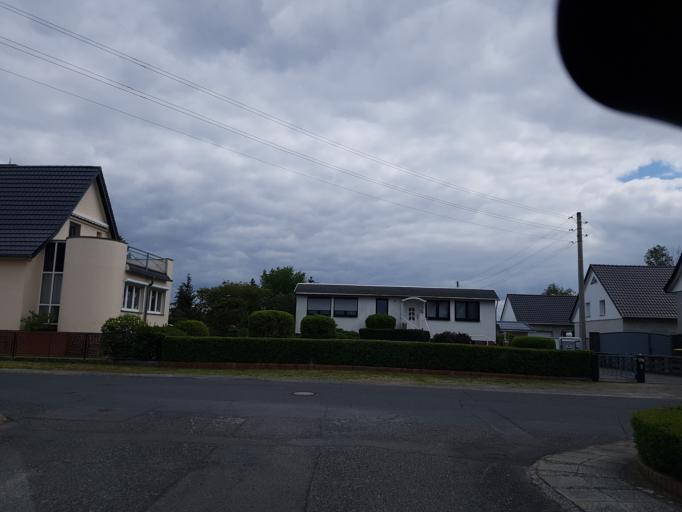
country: DE
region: Brandenburg
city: Altdobern
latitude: 51.6455
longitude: 14.0235
